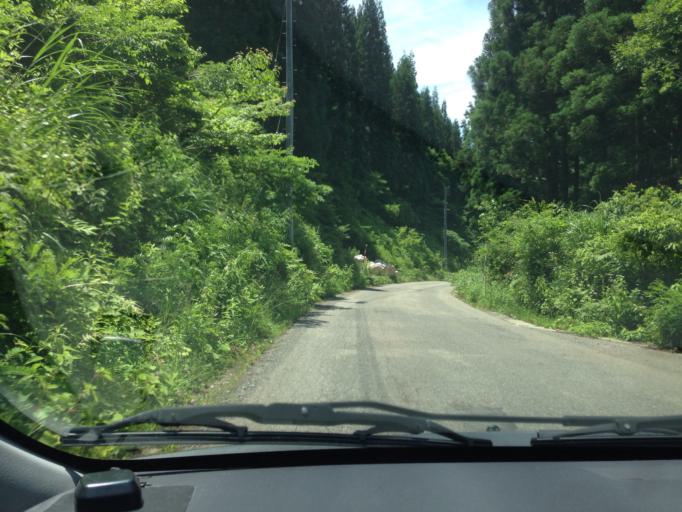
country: JP
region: Fukushima
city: Kitakata
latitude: 37.2553
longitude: 139.7466
